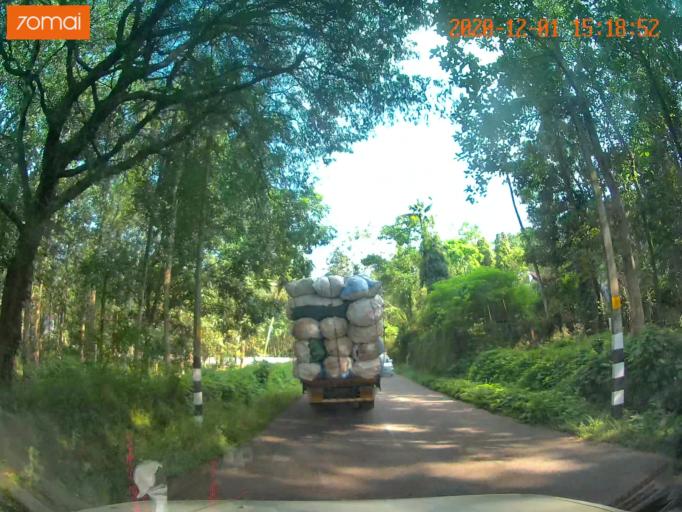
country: IN
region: Kerala
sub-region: Ernakulam
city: Ramamangalam
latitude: 9.9357
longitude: 76.5334
